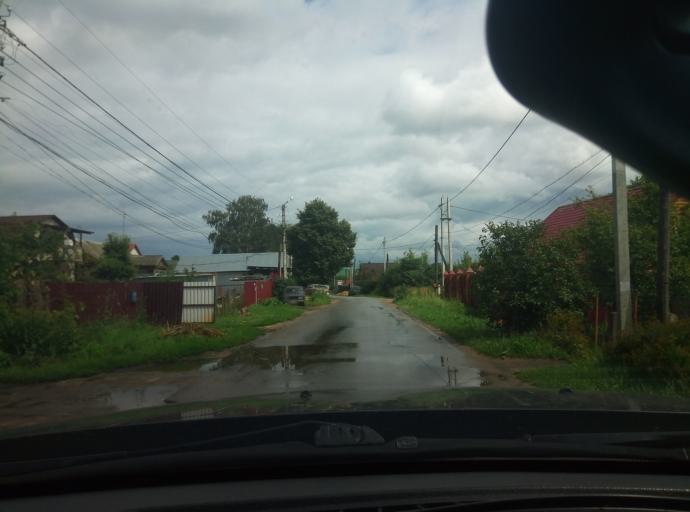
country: RU
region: Tula
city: Novomoskovsk
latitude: 53.9983
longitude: 38.3006
